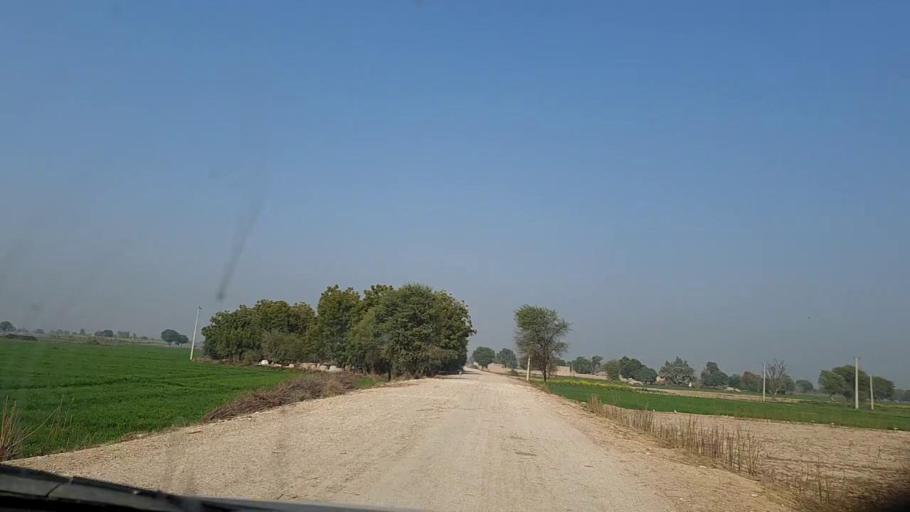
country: PK
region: Sindh
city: Moro
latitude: 26.7759
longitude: 67.9339
